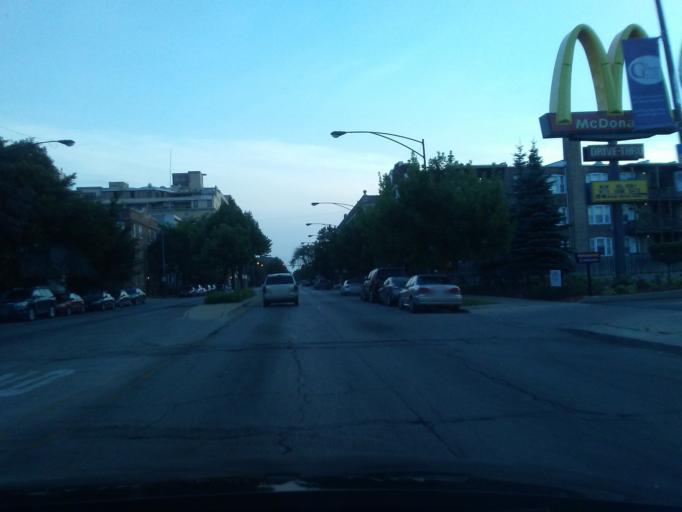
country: US
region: Illinois
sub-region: Cook County
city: Evanston
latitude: 41.9837
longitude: -87.6699
